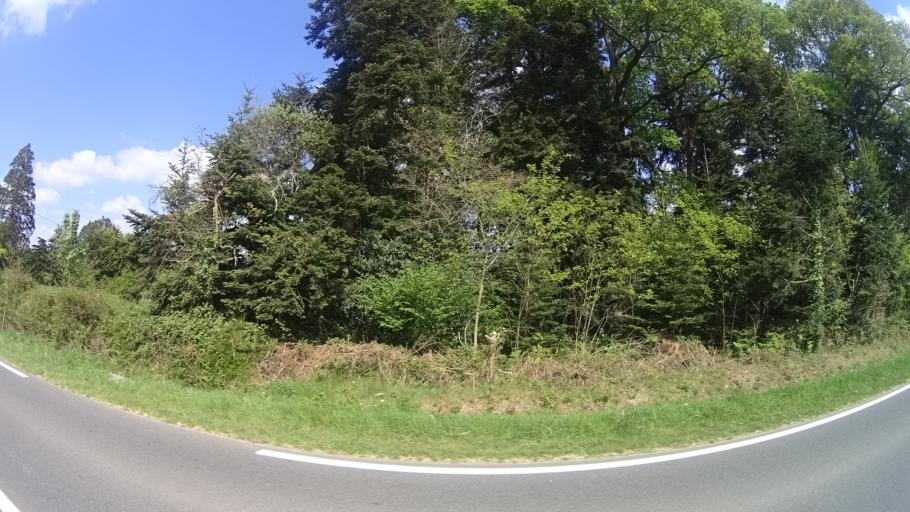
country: FR
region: Brittany
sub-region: Departement du Morbihan
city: Rieux
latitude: 47.6081
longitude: -2.1102
